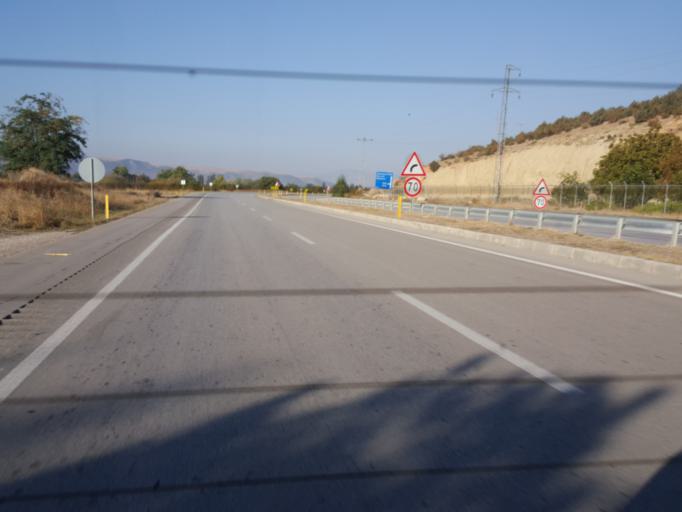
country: TR
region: Amasya
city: Amasya
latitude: 40.5585
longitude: 35.7991
